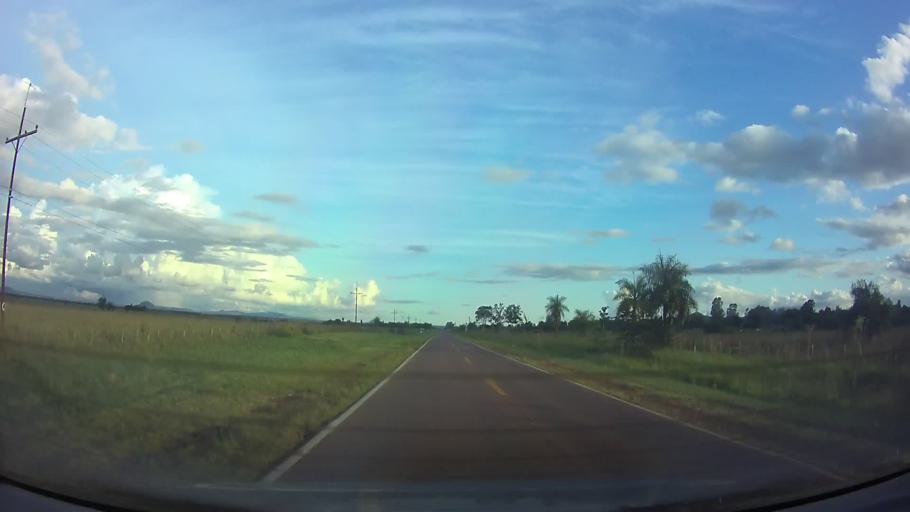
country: PY
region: Paraguari
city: Carapegua
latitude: -25.8135
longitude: -57.1772
